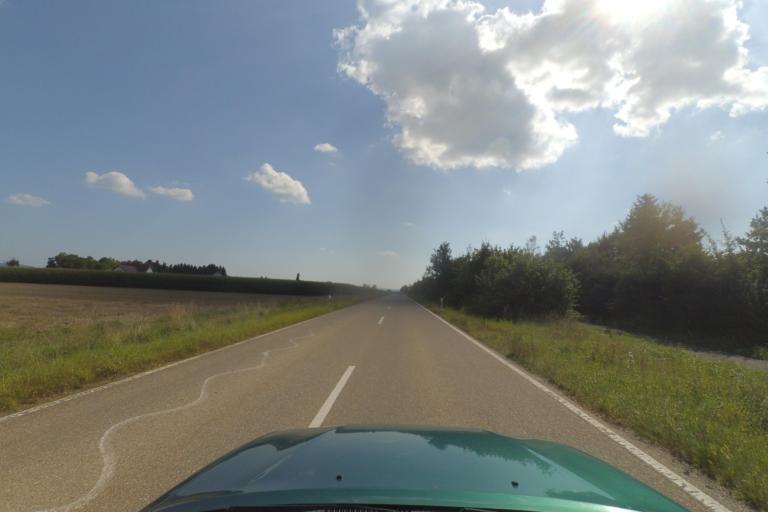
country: DE
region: Bavaria
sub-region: Swabia
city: Munningen
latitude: 48.9164
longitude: 10.6039
